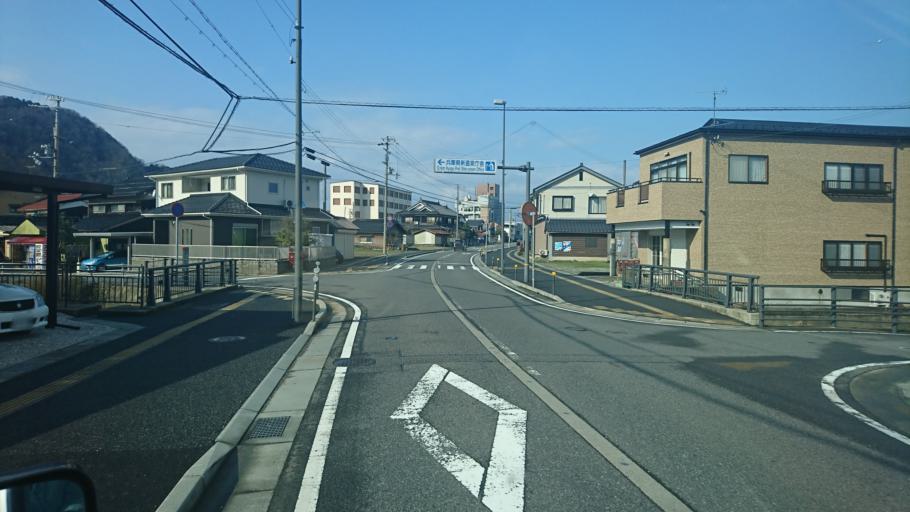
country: JP
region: Tottori
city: Tottori
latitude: 35.6248
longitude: 134.4453
